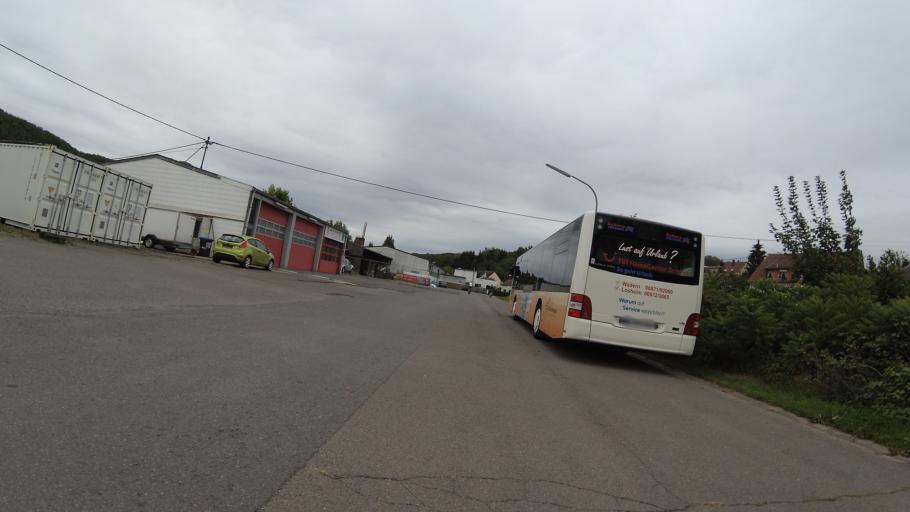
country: DE
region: Saarland
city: Nonnweiler
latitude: 49.5393
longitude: 6.9743
